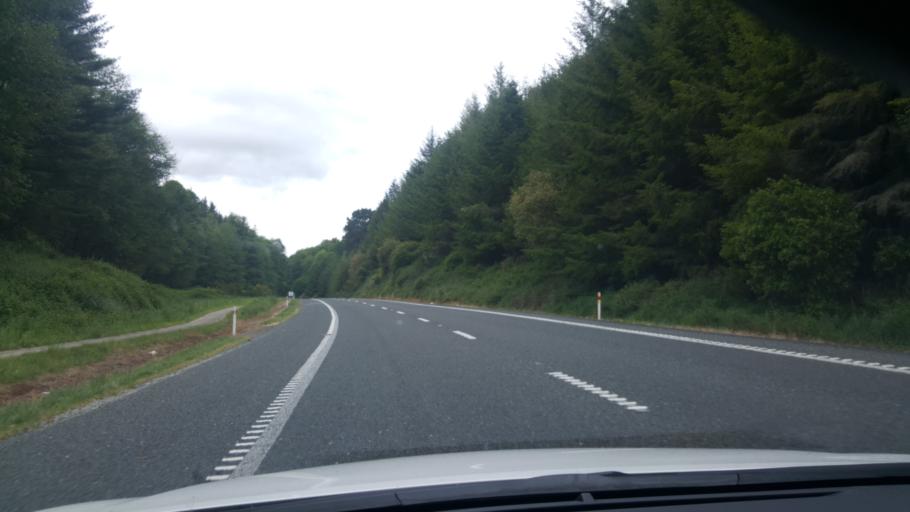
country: NZ
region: Bay of Plenty
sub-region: Rotorua District
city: Rotorua
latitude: -38.2393
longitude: 176.3023
